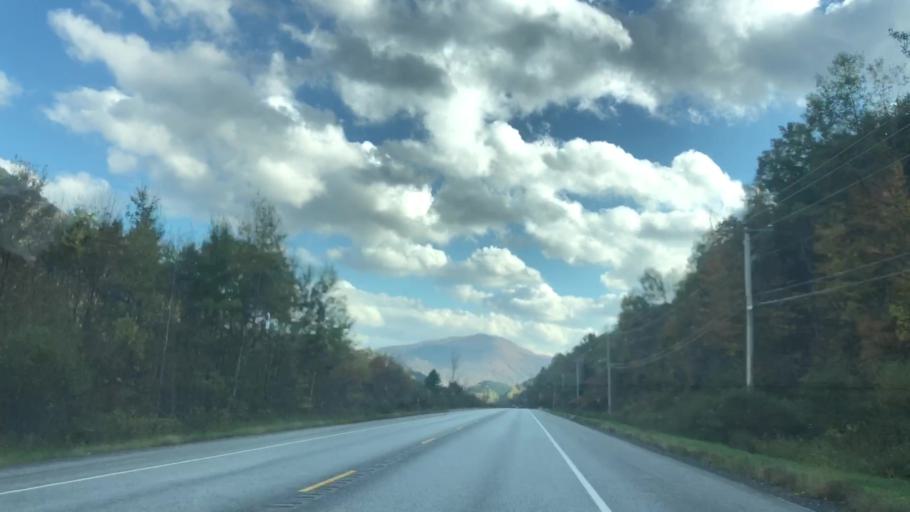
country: US
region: Vermont
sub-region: Rutland County
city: Rutland
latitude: 43.6347
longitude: -72.7655
